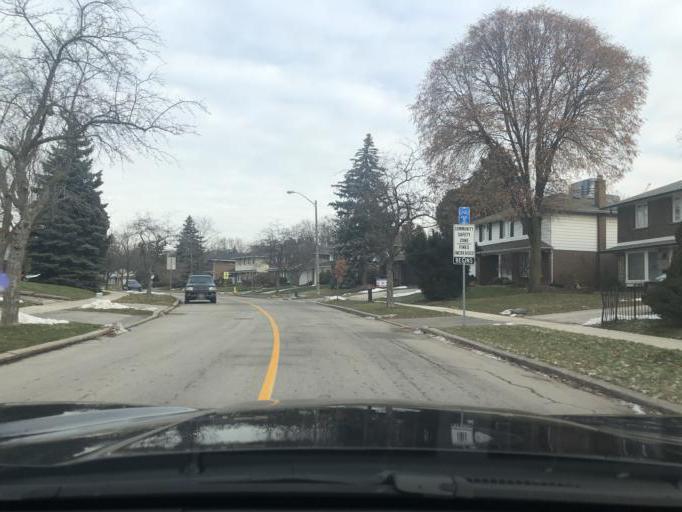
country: CA
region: Ontario
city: Willowdale
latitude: 43.7685
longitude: -79.3506
